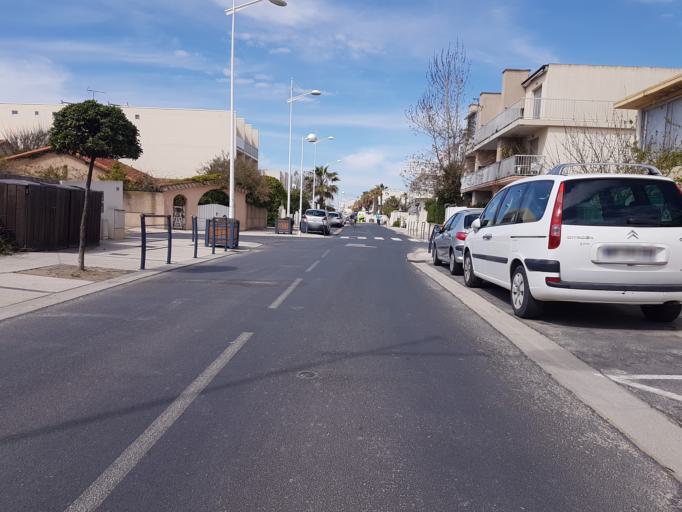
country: FR
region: Languedoc-Roussillon
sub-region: Departement de l'Herault
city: Perols
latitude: 43.5476
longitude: 3.9882
